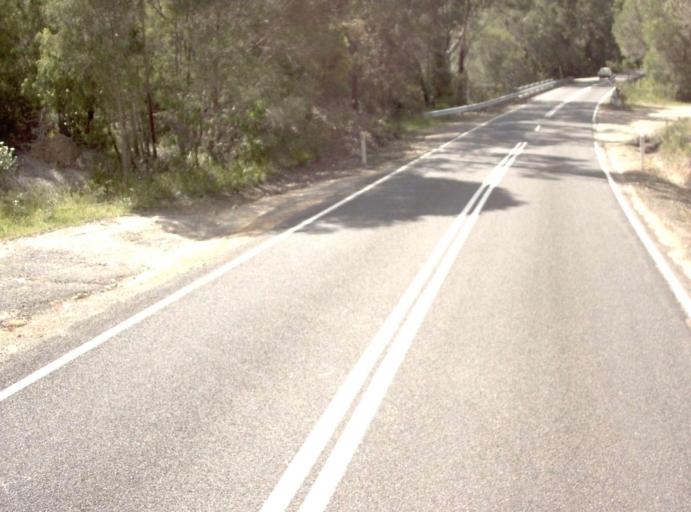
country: AU
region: New South Wales
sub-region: Bega Valley
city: Eden
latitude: -37.5308
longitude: 149.6897
